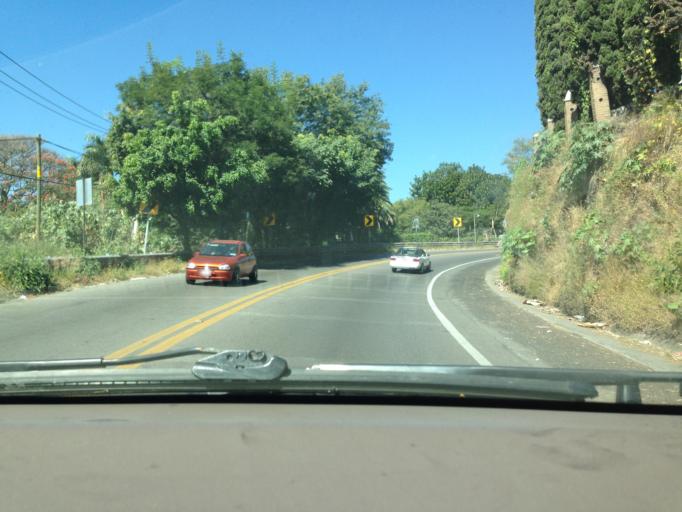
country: MX
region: Morelos
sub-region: Cuernavaca
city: Fraccionamiento Lomas de Ahuatlan
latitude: 18.9720
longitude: -99.2514
